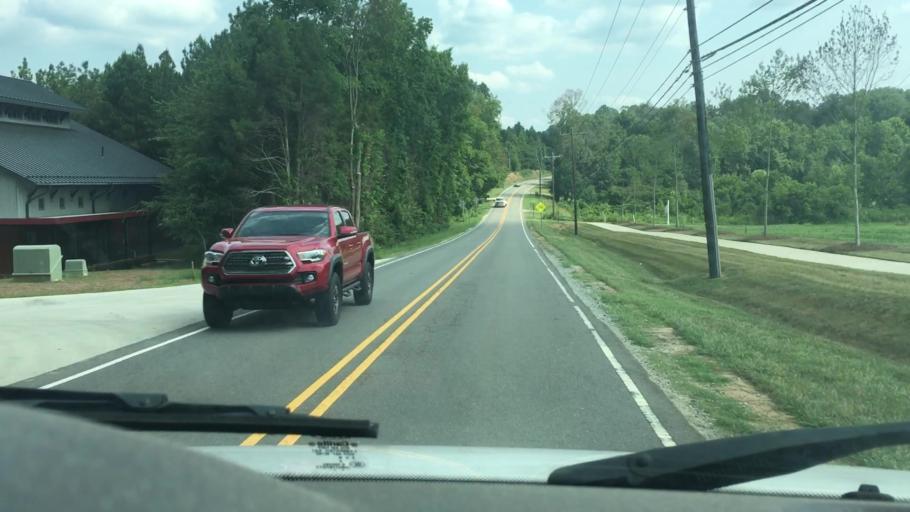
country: US
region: North Carolina
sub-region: Gaston County
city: Davidson
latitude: 35.4745
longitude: -80.8178
